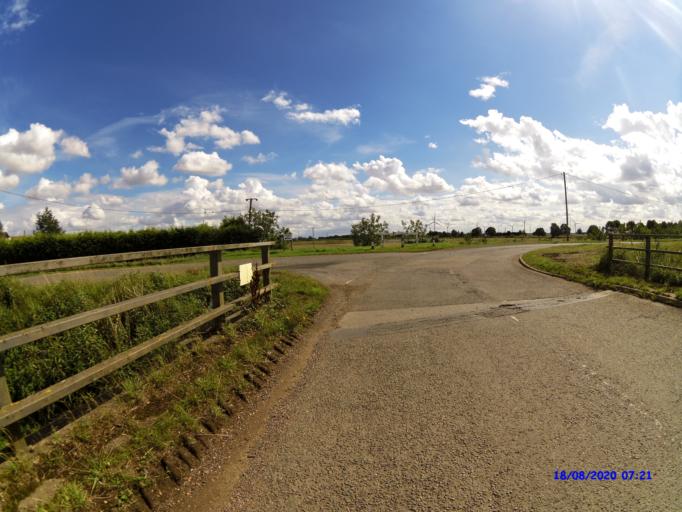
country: GB
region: England
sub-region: Cambridgeshire
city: Whittlesey
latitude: 52.5291
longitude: -0.1022
